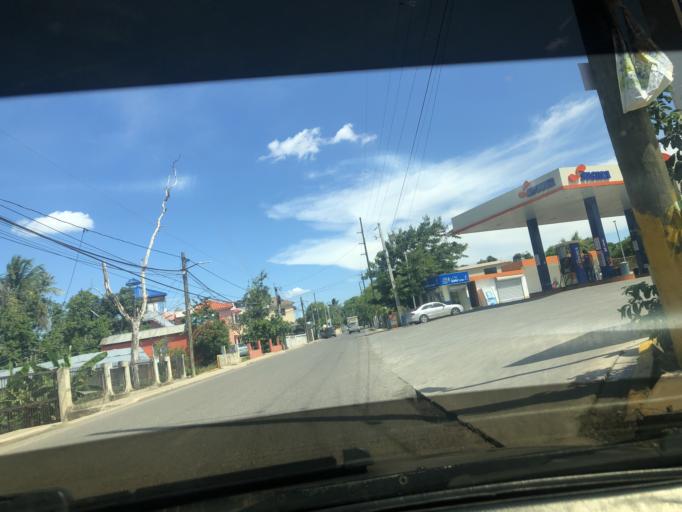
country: DO
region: Santiago
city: Santiago de los Caballeros
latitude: 19.4019
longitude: -70.6701
